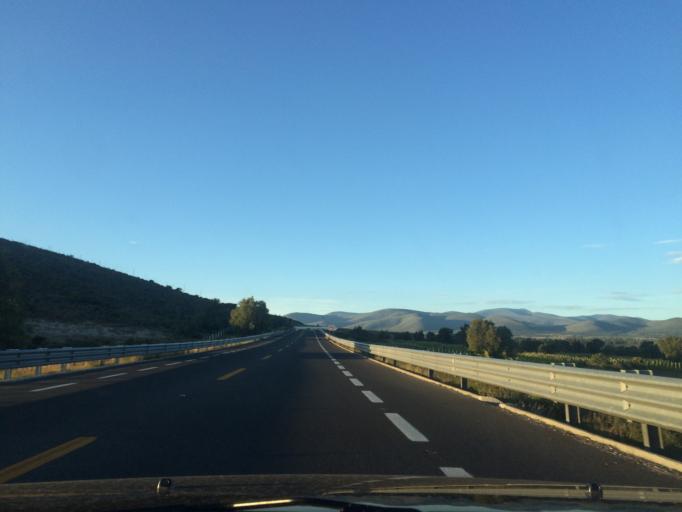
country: MX
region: Puebla
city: Cuacnopalan
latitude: 18.7993
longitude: -97.4897
